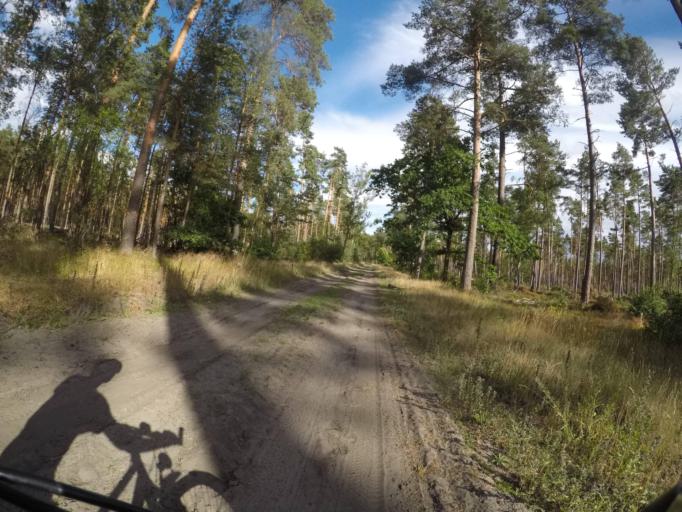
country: DE
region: Lower Saxony
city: Neu Darchau
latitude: 53.2770
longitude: 10.9529
